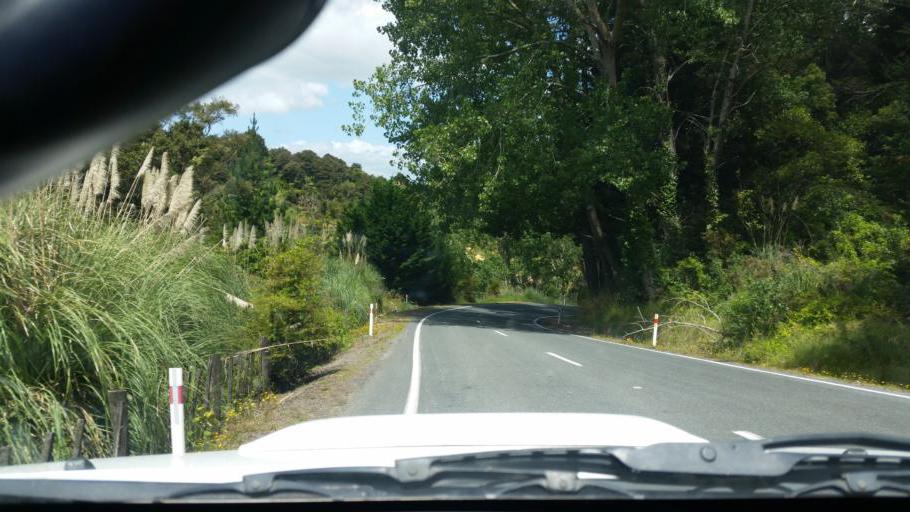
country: NZ
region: Northland
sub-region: Whangarei
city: Ruakaka
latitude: -36.0915
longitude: 174.2423
